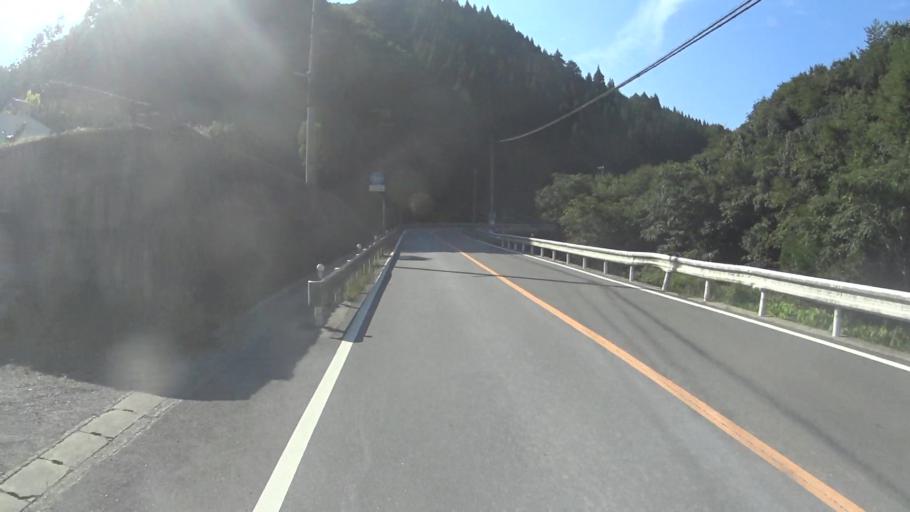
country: JP
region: Kyoto
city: Kameoka
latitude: 34.9416
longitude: 135.5534
